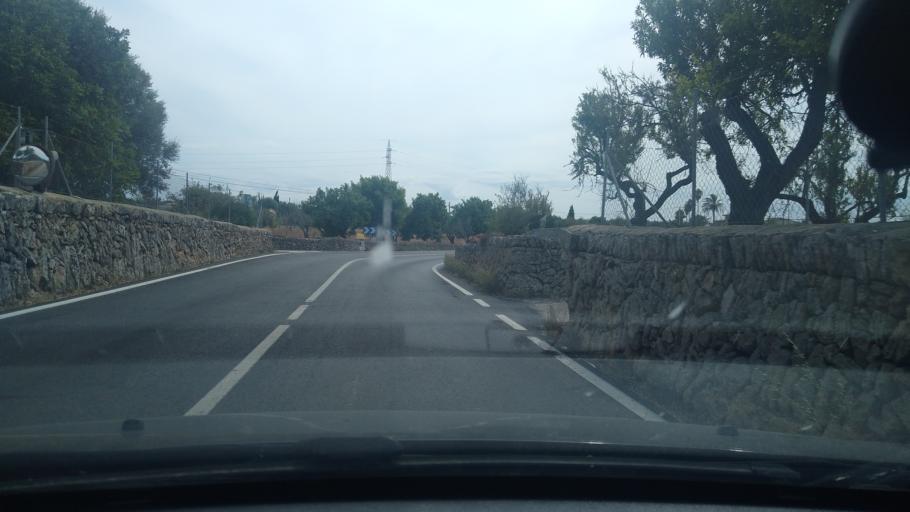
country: ES
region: Balearic Islands
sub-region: Illes Balears
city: Santa Margalida
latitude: 39.7245
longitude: 3.1150
